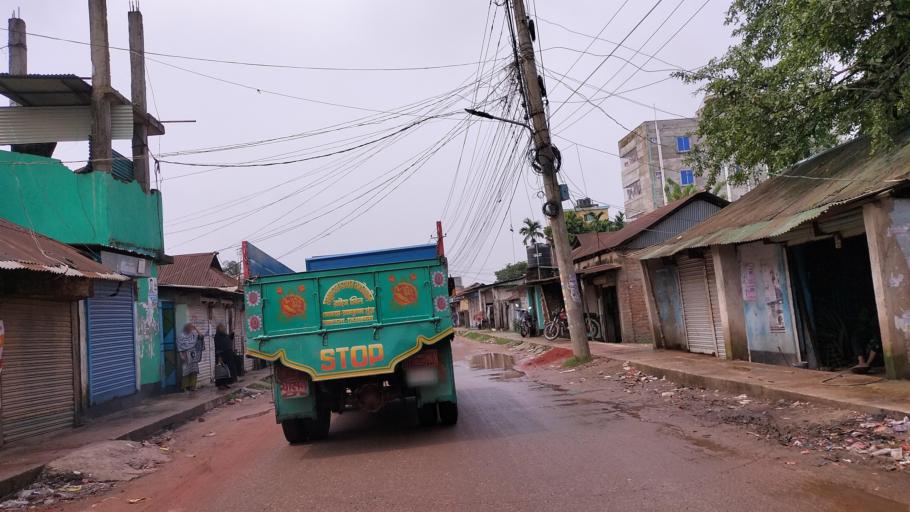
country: BD
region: Dhaka
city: Netrakona
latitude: 24.8887
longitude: 90.7384
